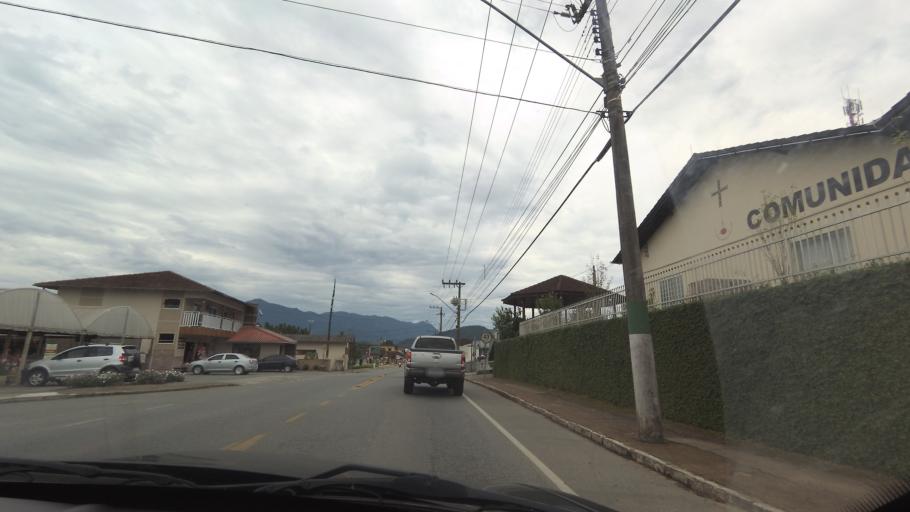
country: BR
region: Santa Catarina
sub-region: Schroeder
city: Schroeder
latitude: -26.4124
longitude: -49.0746
